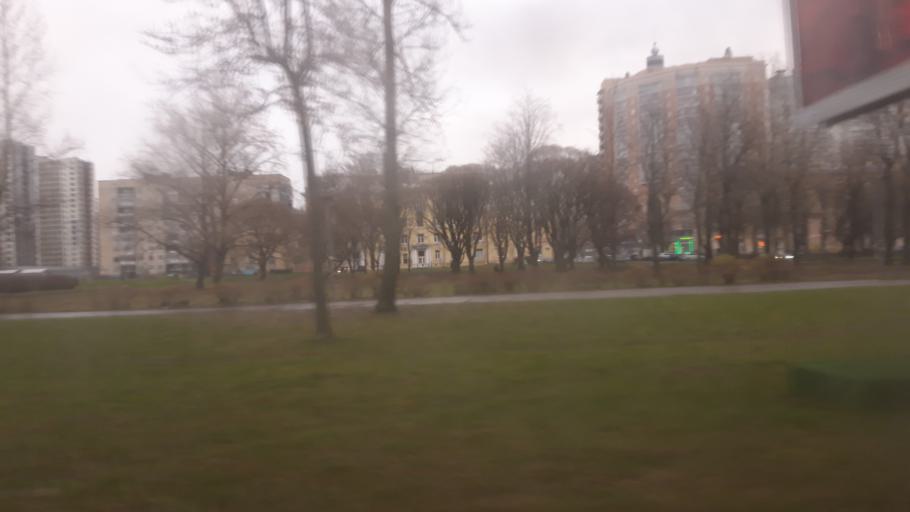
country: RU
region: St.-Petersburg
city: Kupchino
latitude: 59.8288
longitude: 30.3231
